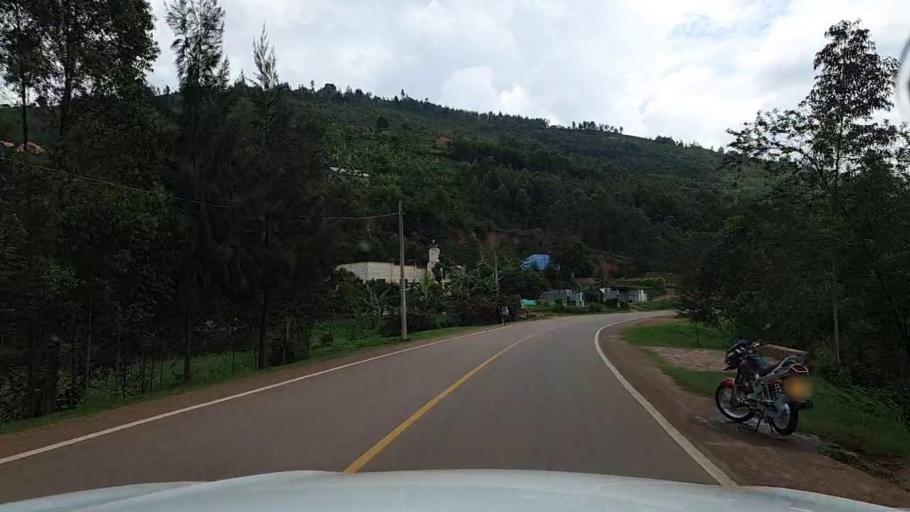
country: RW
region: Kigali
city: Kigali
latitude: -1.8117
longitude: 30.0983
